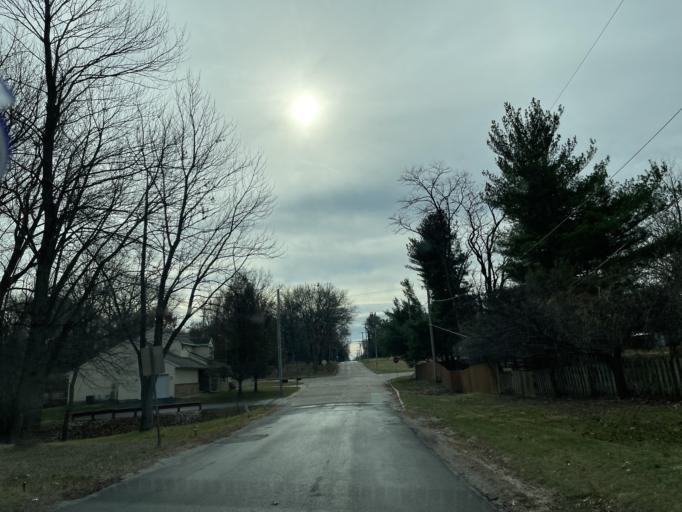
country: US
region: Illinois
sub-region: Sangamon County
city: Leland Grove
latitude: 39.8021
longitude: -89.7298
